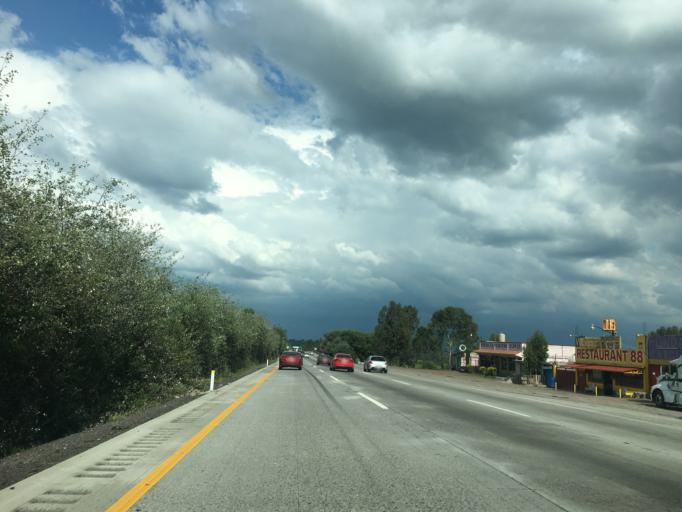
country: MX
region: Mexico
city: San Francisco Soyaniquilpan
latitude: 19.9927
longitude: -99.4706
